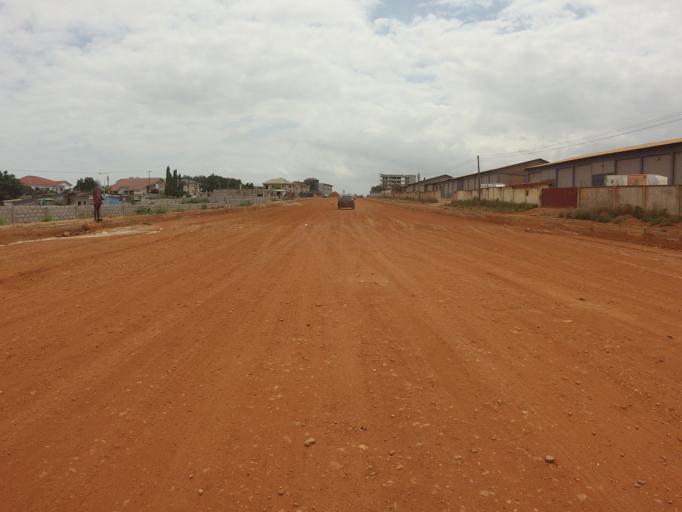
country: GH
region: Greater Accra
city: Medina Estates
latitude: 5.6265
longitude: -0.1489
